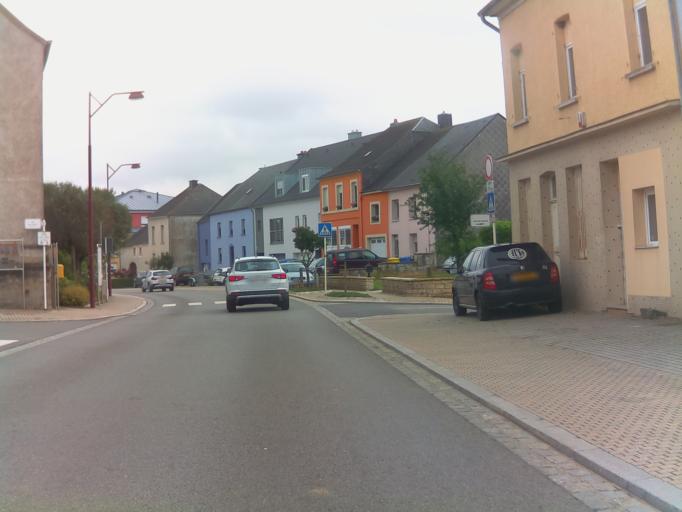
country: LU
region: Luxembourg
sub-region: Canton de Capellen
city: Steinfort
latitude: 49.6486
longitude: 5.9298
